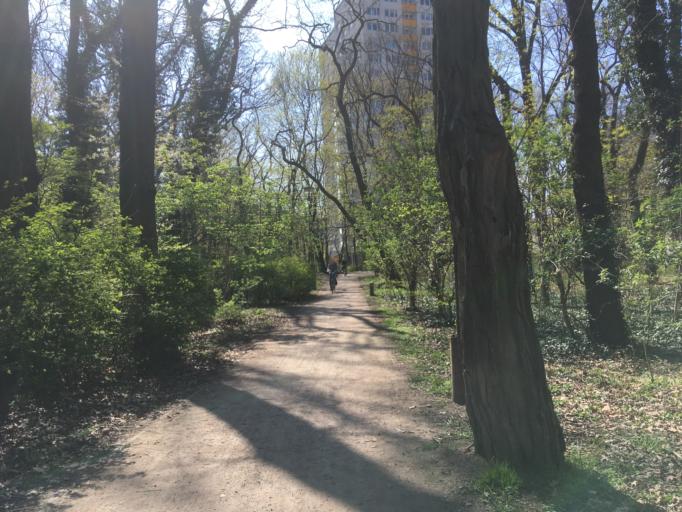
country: DE
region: Berlin
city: Friedrichsfelde
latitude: 52.4975
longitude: 13.5165
